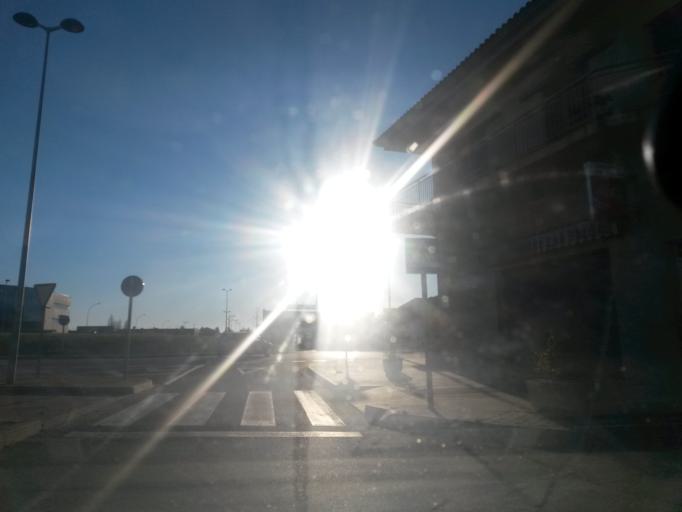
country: ES
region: Catalonia
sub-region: Provincia de Girona
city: Salt
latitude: 41.9583
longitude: 2.8009
